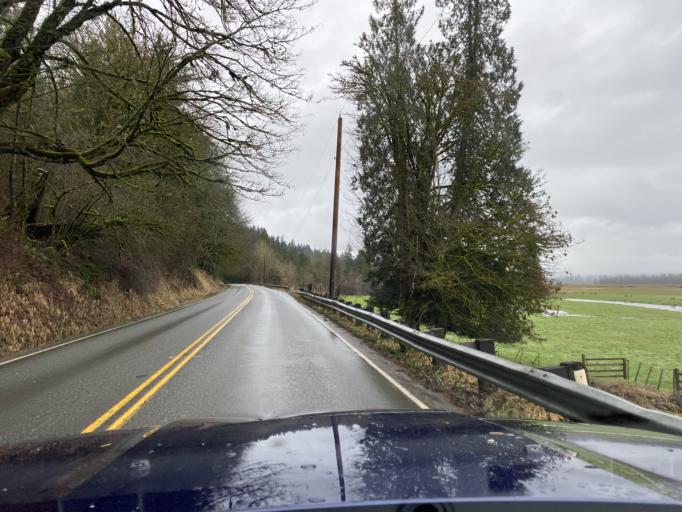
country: US
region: Washington
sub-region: King County
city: Duvall
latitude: 47.7520
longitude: -122.0043
